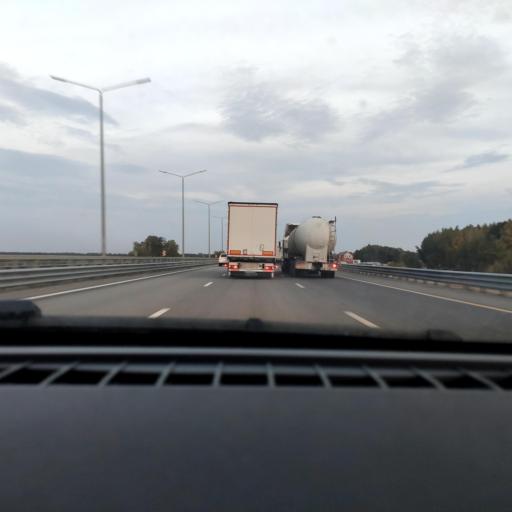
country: RU
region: Voronezj
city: Somovo
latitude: 51.7901
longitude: 39.2759
